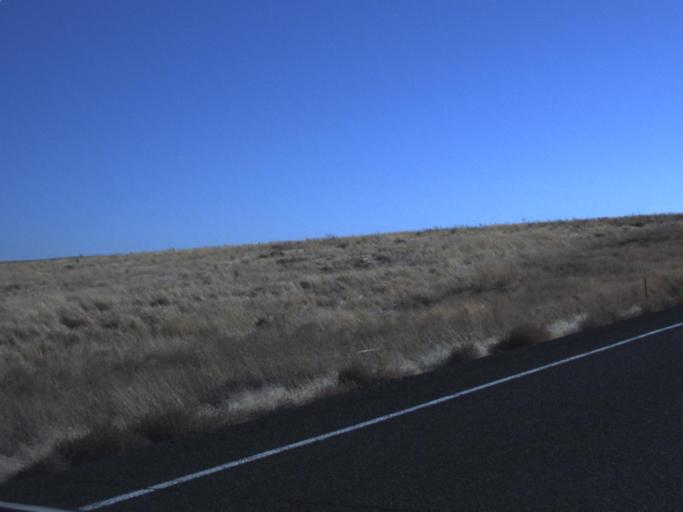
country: US
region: Washington
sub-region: Franklin County
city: Connell
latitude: 46.7188
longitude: -118.5481
